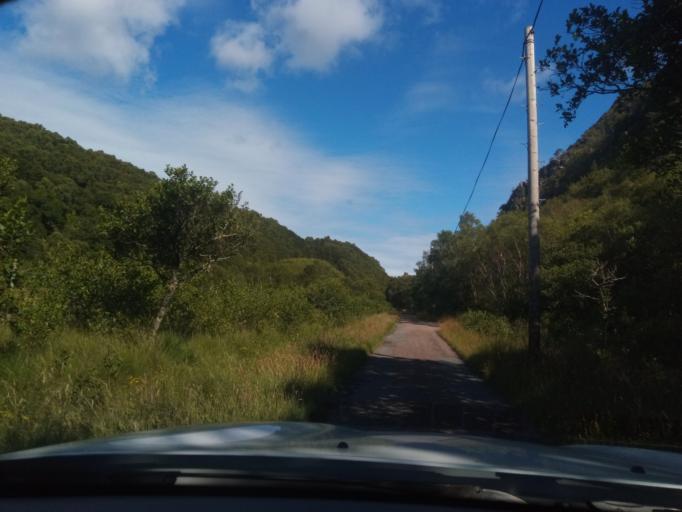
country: GB
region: Scotland
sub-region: Argyll and Bute
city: Isle Of Mull
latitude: 56.7662
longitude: -5.8215
